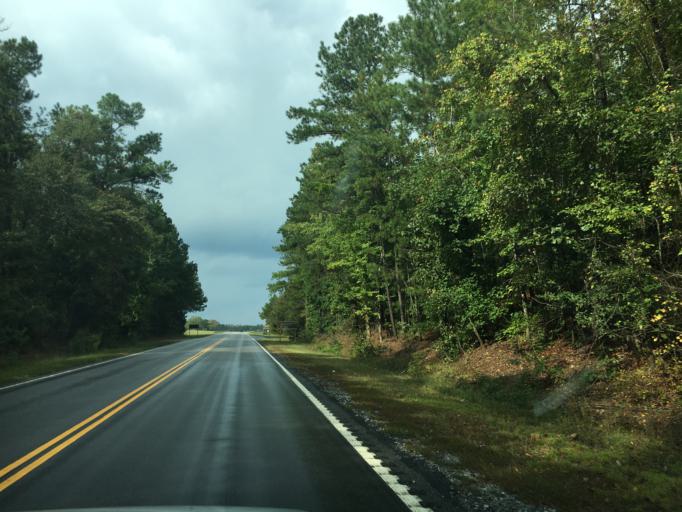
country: US
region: Georgia
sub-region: Hart County
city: Hartwell
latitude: 34.3619
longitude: -82.8139
